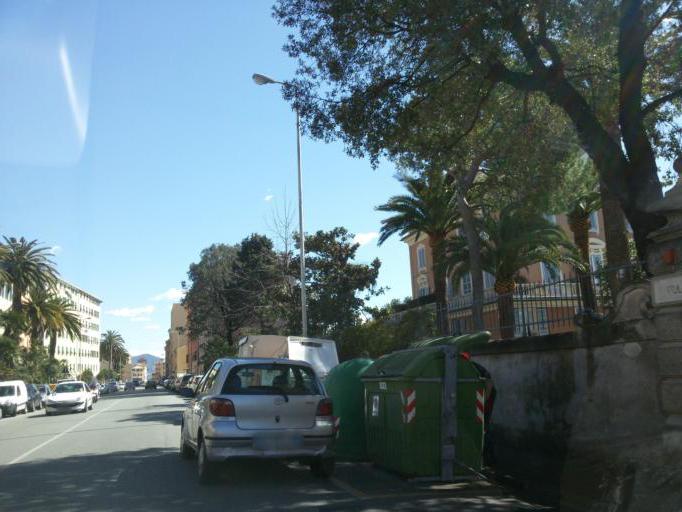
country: IT
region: Liguria
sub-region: Provincia di Genova
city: Bogliasco
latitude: 44.3838
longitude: 9.0221
